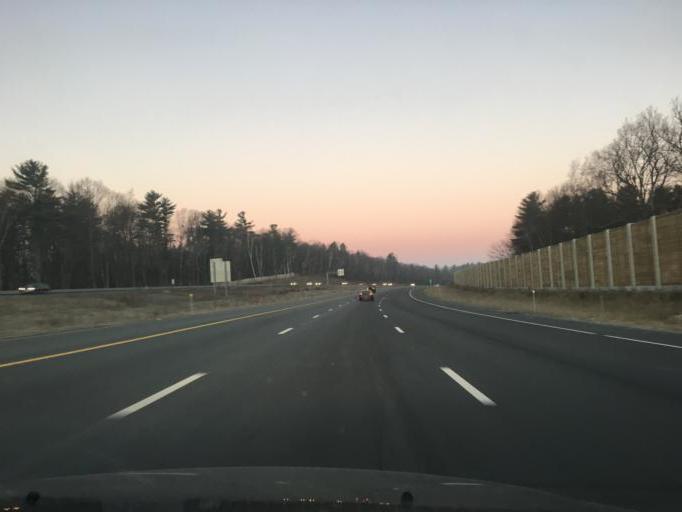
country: US
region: New Hampshire
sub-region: Rockingham County
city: Windham
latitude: 42.7858
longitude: -71.2643
